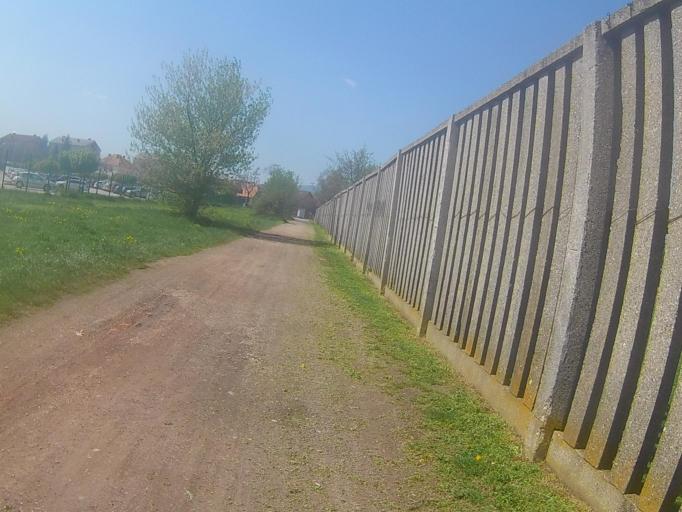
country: SI
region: Maribor
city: Maribor
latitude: 46.5492
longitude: 15.6316
